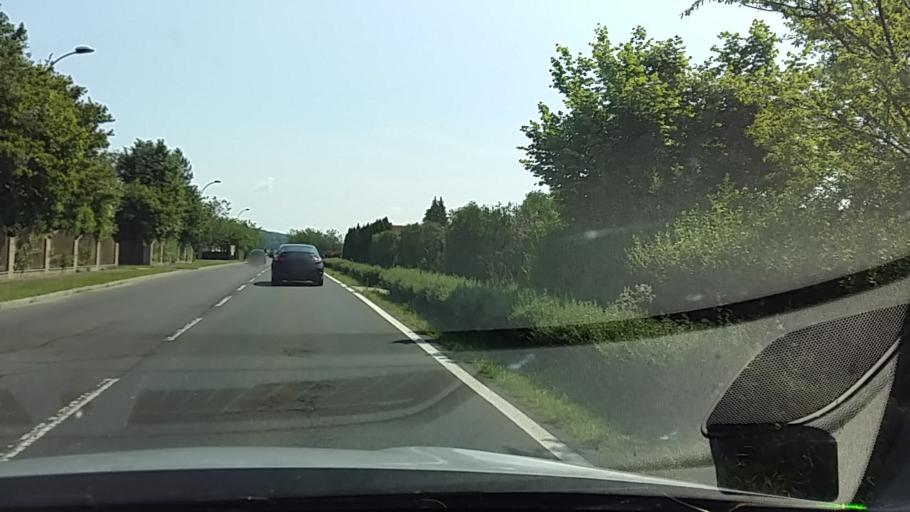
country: AT
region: Burgenland
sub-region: Politischer Bezirk Jennersdorf
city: Weichselbaum
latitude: 46.9418
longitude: 16.1885
